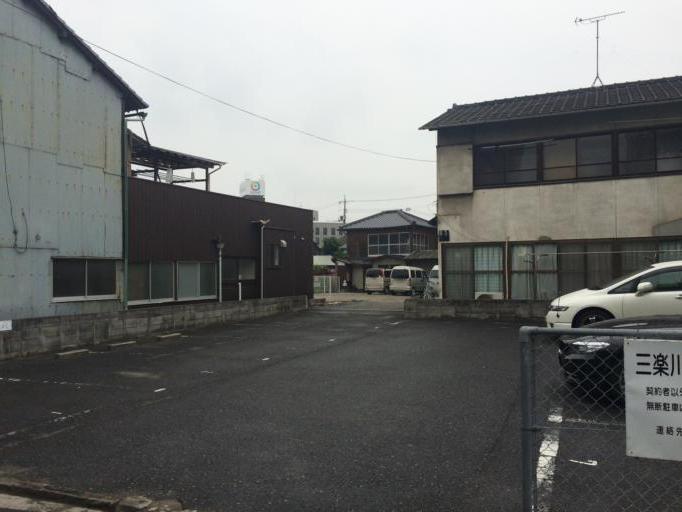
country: JP
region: Okayama
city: Kurashiki
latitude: 34.5978
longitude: 133.7654
